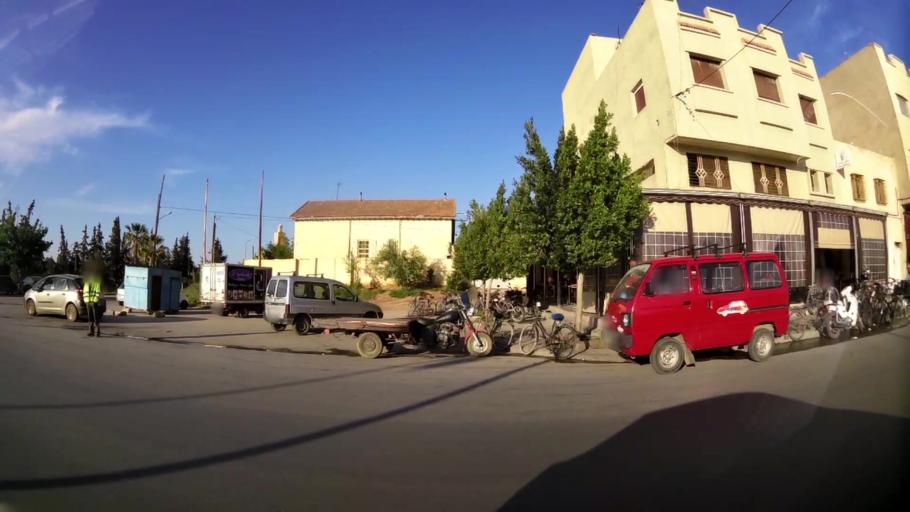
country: MA
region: Oriental
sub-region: Oujda-Angad
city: Oujda
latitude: 34.6979
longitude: -1.9100
